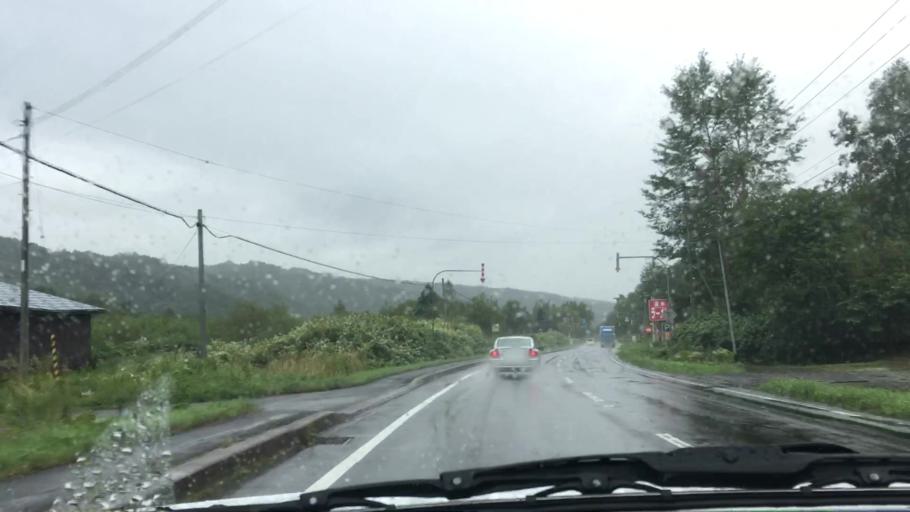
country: JP
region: Hokkaido
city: Niseko Town
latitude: 42.8086
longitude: 141.0002
